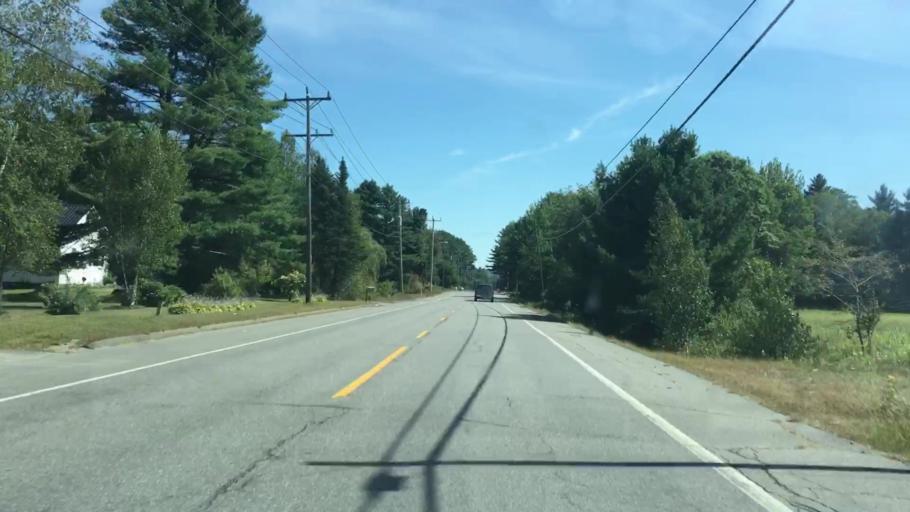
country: US
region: Maine
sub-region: Piscataquis County
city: Milo
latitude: 45.2415
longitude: -68.9711
